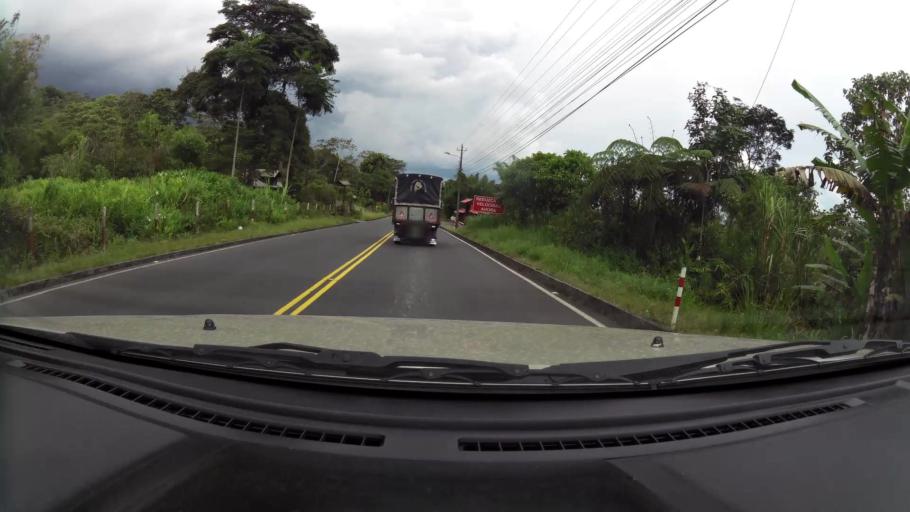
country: EC
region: Pastaza
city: Puyo
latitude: -1.5065
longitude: -78.0283
